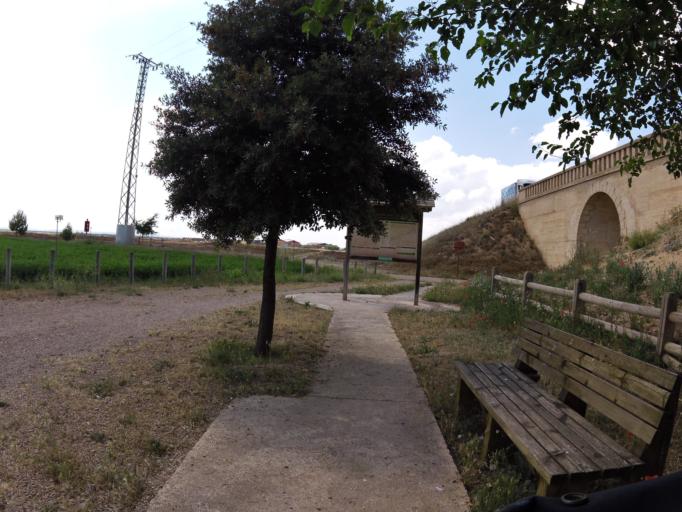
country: ES
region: Castille-La Mancha
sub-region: Provincia de Albacete
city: Pozuelo
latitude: 38.9159
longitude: -2.0113
